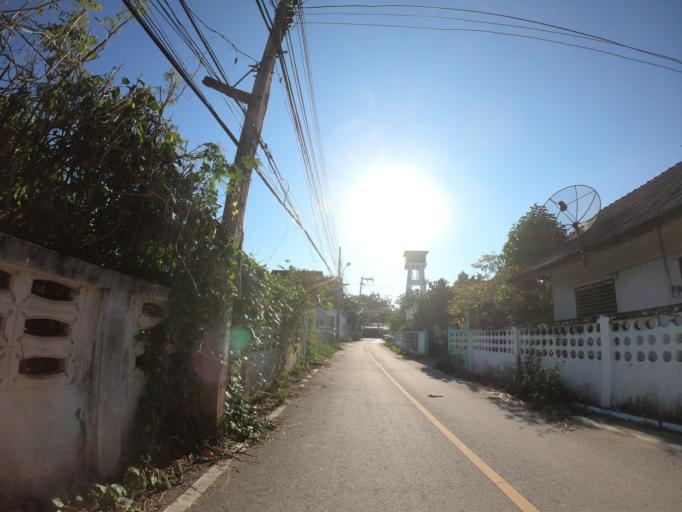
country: TH
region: Chiang Mai
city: San Sai
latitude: 18.8282
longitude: 99.0310
